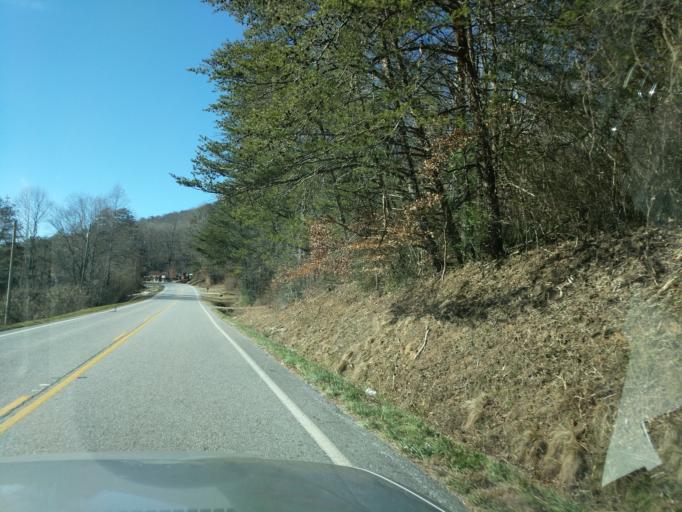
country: US
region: Georgia
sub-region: Rabun County
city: Clayton
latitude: 34.8656
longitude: -83.4867
